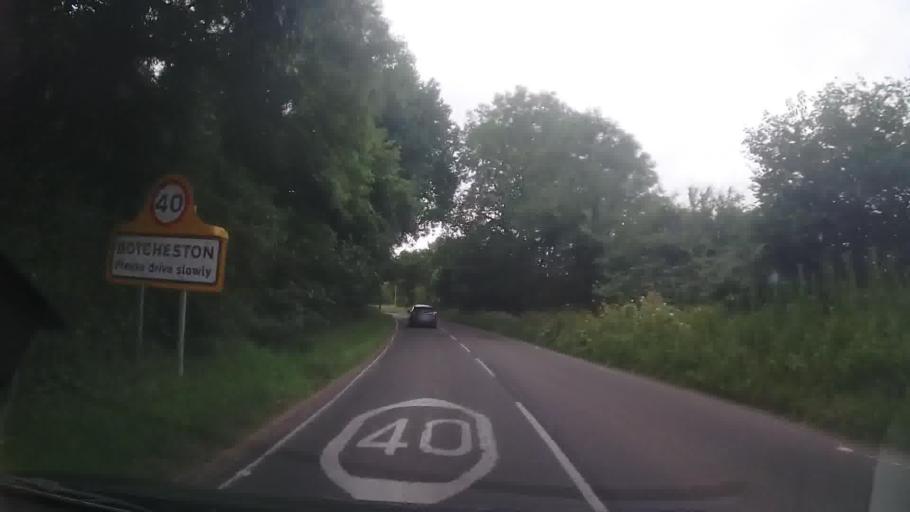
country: GB
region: England
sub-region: Leicestershire
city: Desford
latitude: 52.6494
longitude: -1.2906
